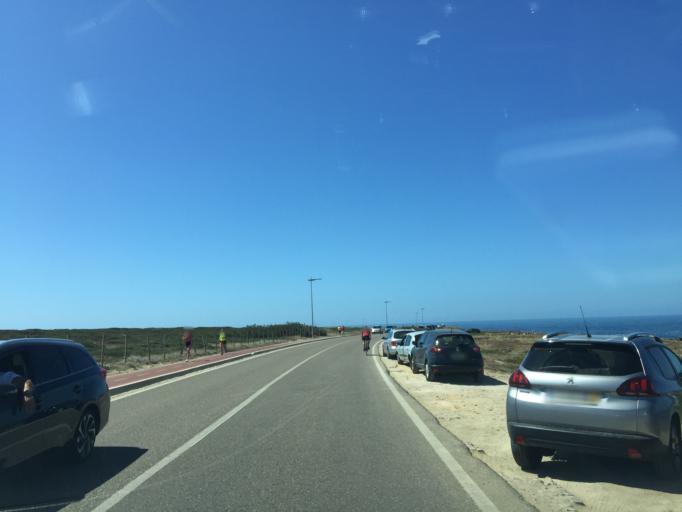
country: PT
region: Lisbon
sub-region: Cascais
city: Cascais
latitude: 38.7173
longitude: -9.4804
